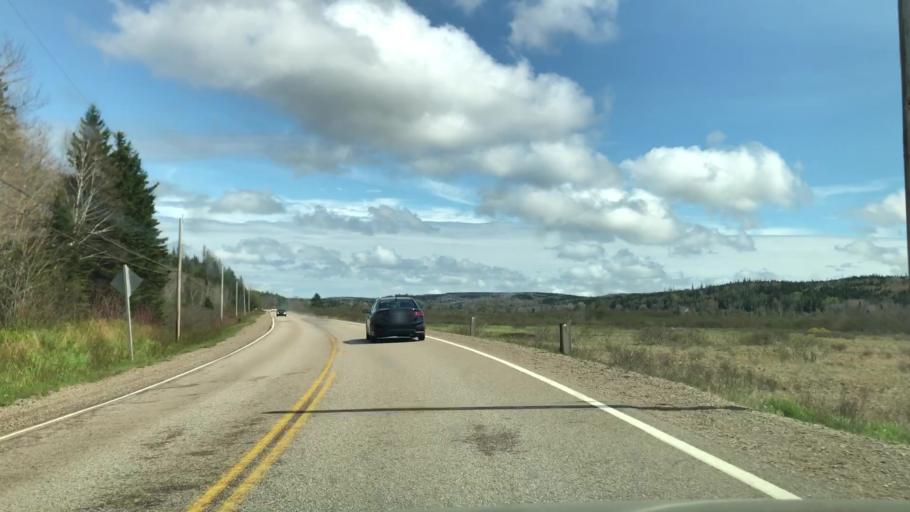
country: CA
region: Nova Scotia
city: Antigonish
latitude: 45.1958
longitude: -62.0007
